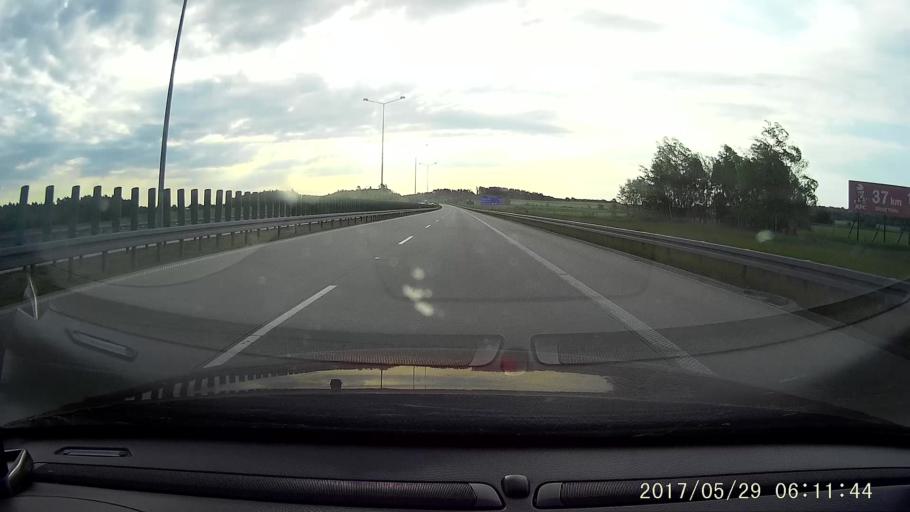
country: PL
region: Lower Silesian Voivodeship
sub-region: Powiat lubanski
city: Pisarzowice
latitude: 51.2163
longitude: 15.2485
